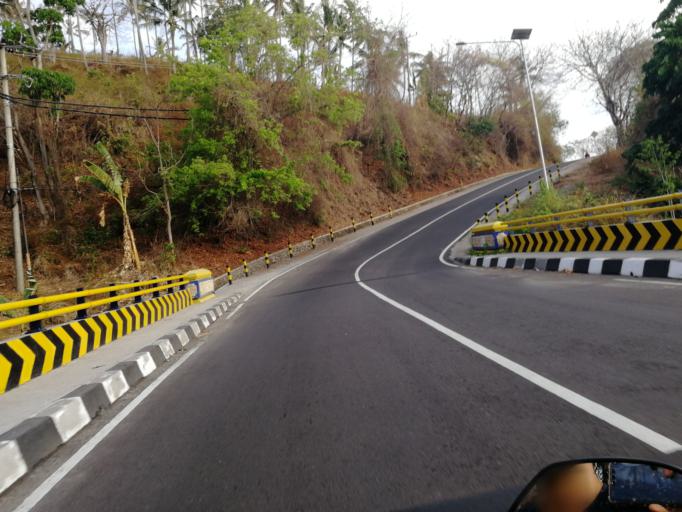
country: ID
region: West Nusa Tenggara
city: Karangsubagan
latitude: -8.4634
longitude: 116.0367
